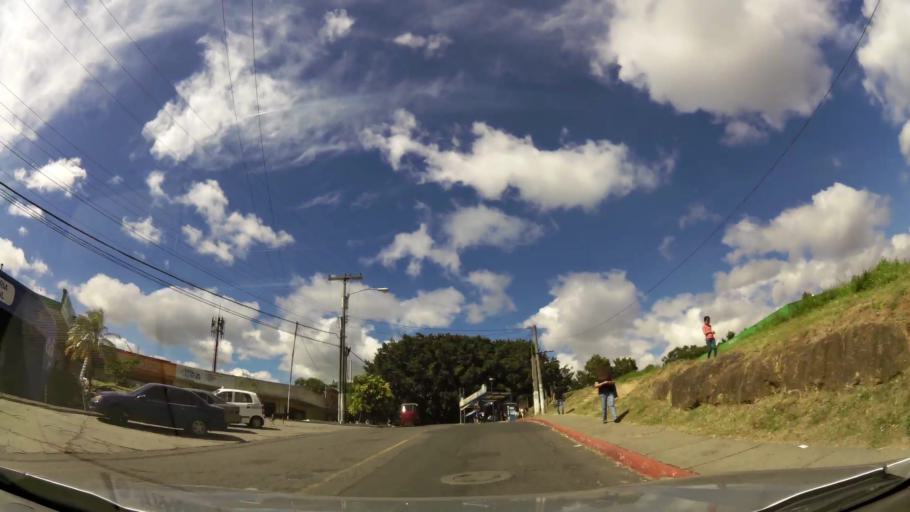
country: GT
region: Guatemala
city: Villa Nueva
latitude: 14.5458
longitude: -90.5521
